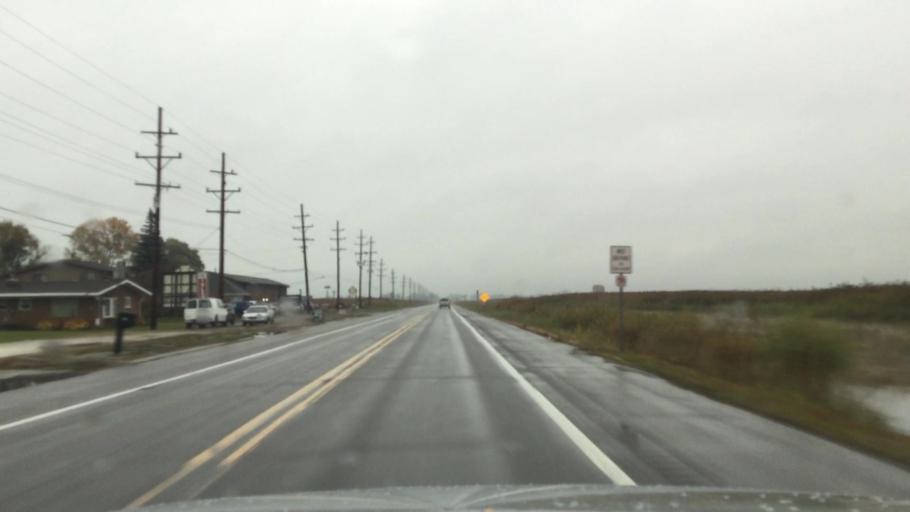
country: US
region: Michigan
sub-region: Saint Clair County
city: Pearl Beach
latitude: 42.6358
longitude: -82.6162
